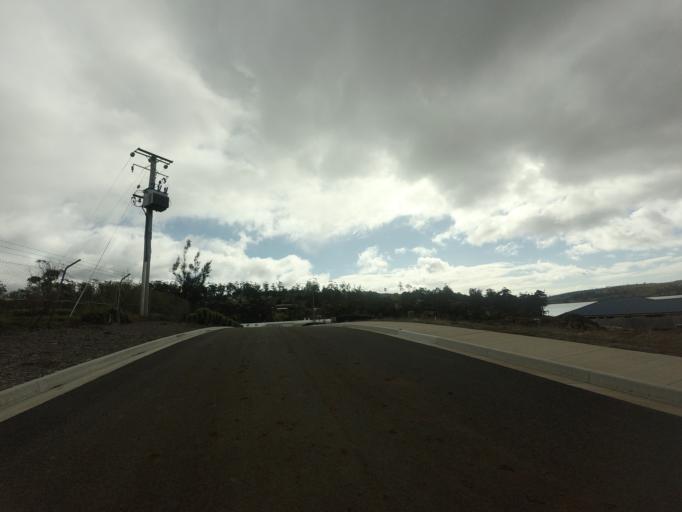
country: AU
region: Tasmania
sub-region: Sorell
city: Sorell
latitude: -42.5432
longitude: 147.9139
